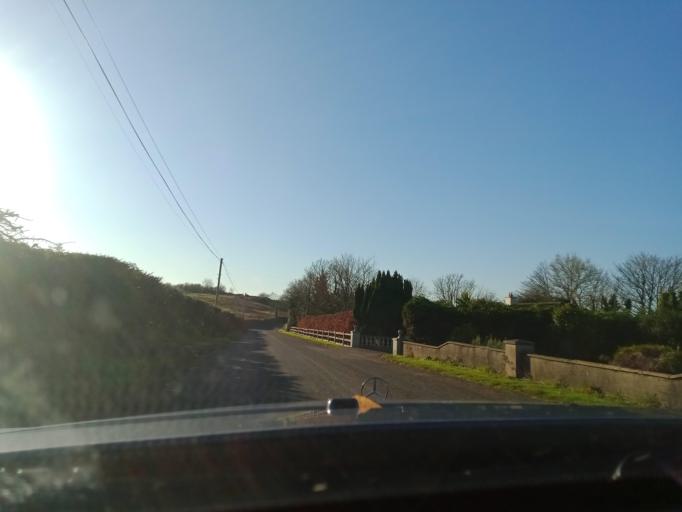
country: IE
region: Leinster
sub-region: Kilkenny
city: Mooncoin
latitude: 52.2931
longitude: -7.2271
